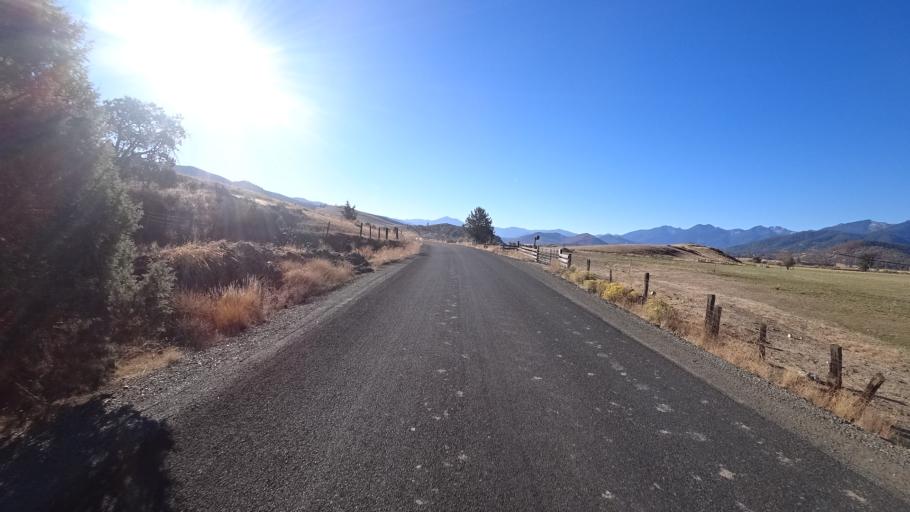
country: US
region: California
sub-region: Siskiyou County
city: Yreka
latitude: 41.4468
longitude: -122.8460
